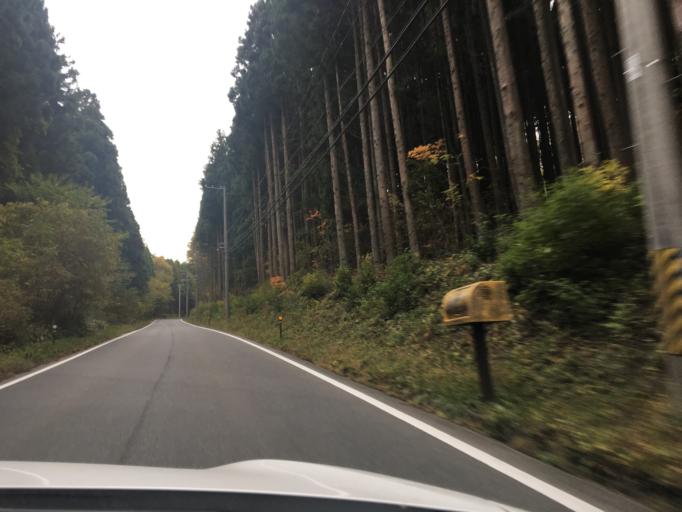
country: JP
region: Fukushima
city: Iwaki
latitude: 37.1121
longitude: 140.7799
